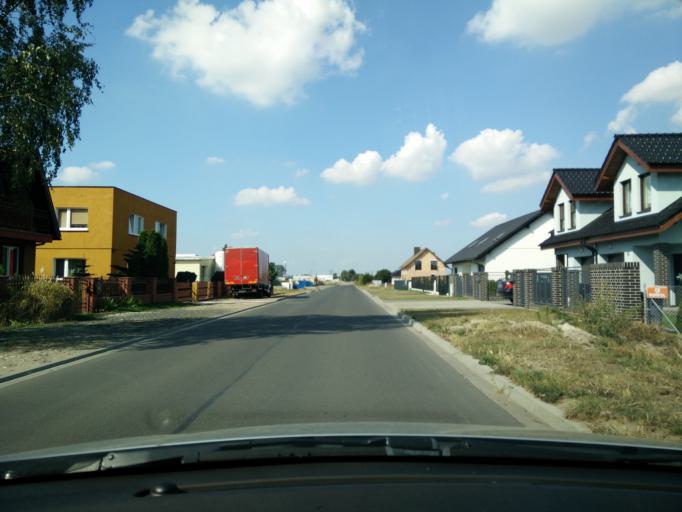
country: PL
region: Greater Poland Voivodeship
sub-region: Powiat sredzki
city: Sroda Wielkopolska
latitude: 52.2376
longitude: 17.2511
